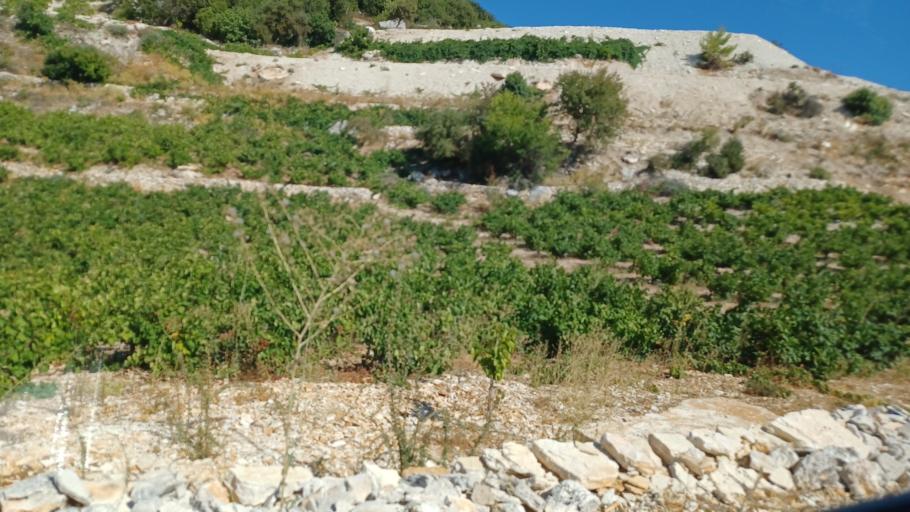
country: CY
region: Limassol
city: Pachna
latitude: 34.9061
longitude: 32.6400
